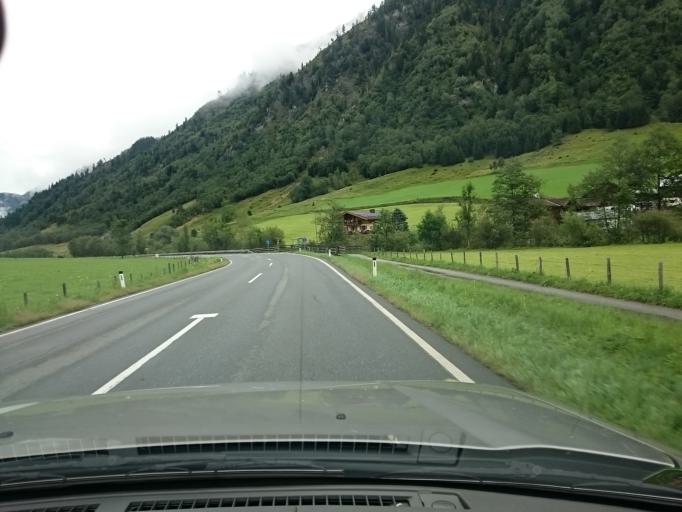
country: AT
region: Salzburg
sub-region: Politischer Bezirk Zell am See
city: Bruck an der Grossglocknerstrasse
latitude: 47.2437
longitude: 12.8262
